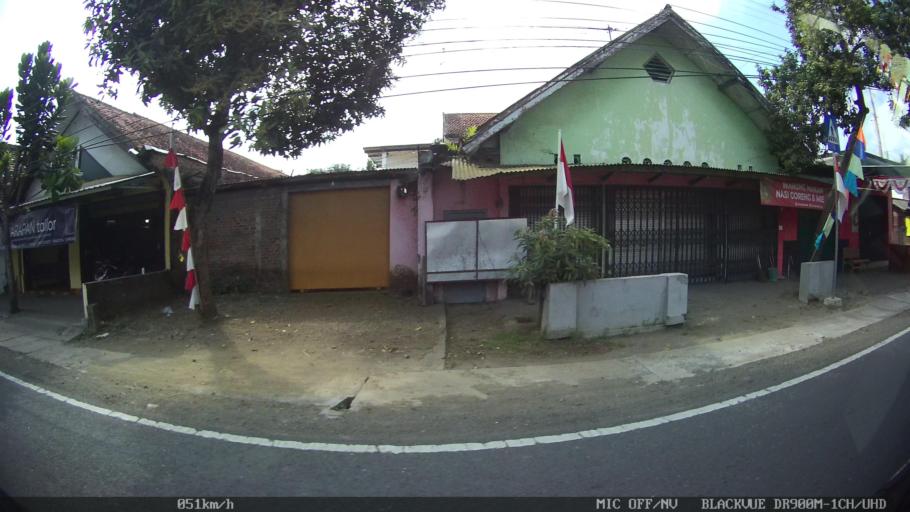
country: ID
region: Daerah Istimewa Yogyakarta
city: Godean
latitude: -7.8400
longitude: 110.2197
